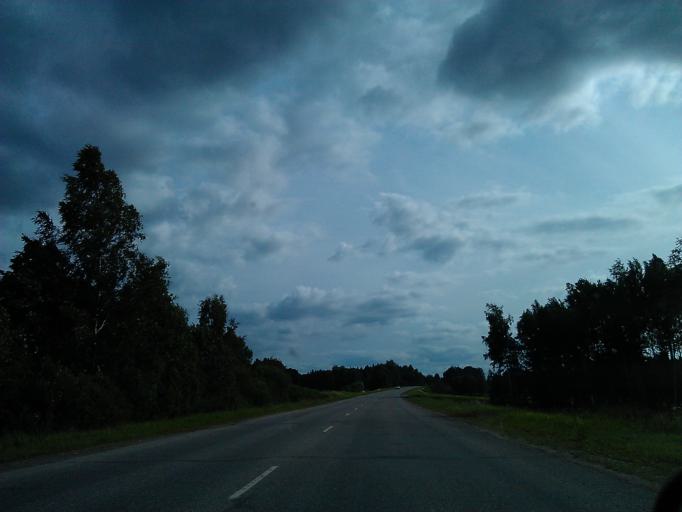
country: LV
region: Cesu Rajons
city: Cesis
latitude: 57.2895
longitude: 25.3009
